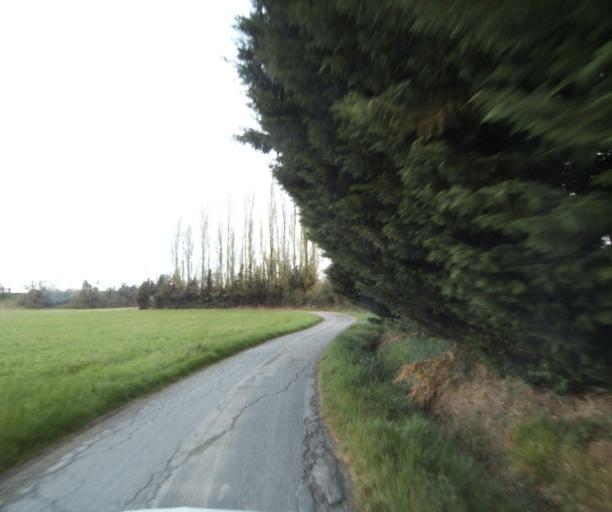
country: FR
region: Midi-Pyrenees
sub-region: Departement de l'Ariege
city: Saverdun
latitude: 43.2266
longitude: 1.5950
